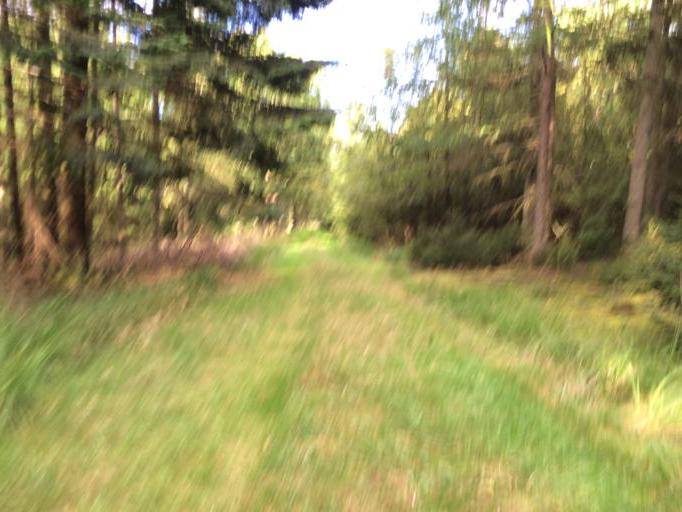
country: DK
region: Central Jutland
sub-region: Holstebro Kommune
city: Ulfborg
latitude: 56.2598
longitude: 8.4410
